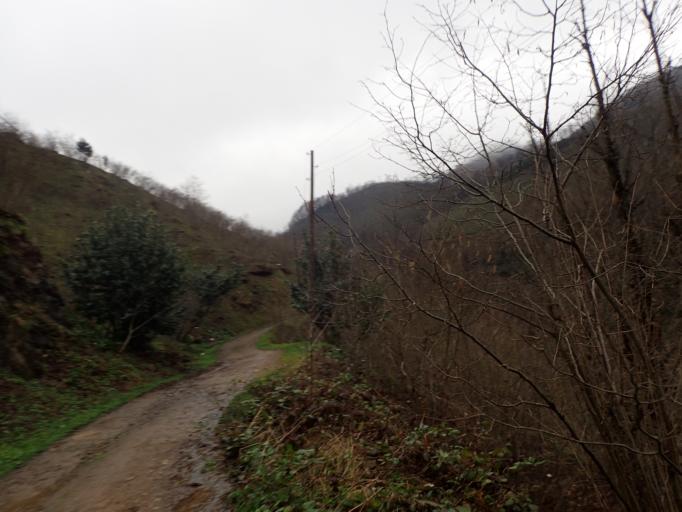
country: TR
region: Ordu
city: Camas
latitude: 40.8629
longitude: 37.5070
